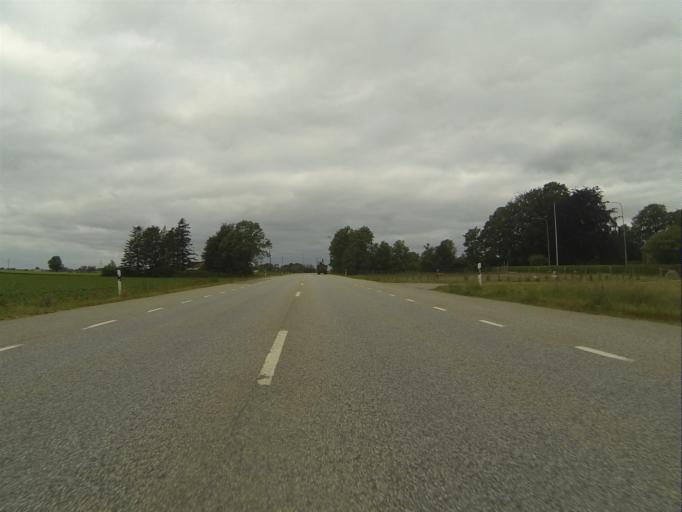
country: SE
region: Skane
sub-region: Staffanstorps Kommun
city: Hjaerup
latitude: 55.6425
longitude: 13.1385
